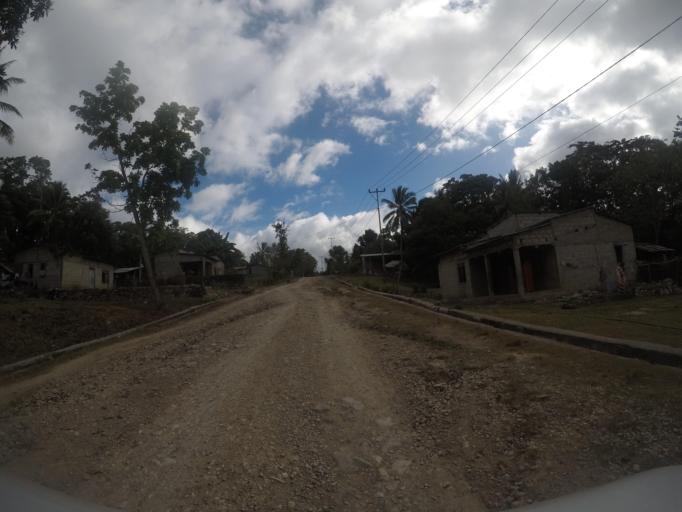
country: TL
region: Lautem
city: Lospalos
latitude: -8.5661
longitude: 126.8862
